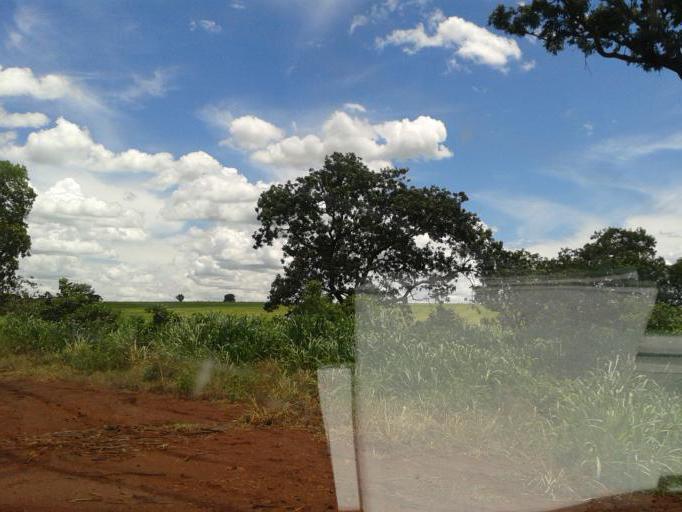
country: BR
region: Minas Gerais
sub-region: Santa Vitoria
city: Santa Vitoria
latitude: -18.6958
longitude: -50.1991
